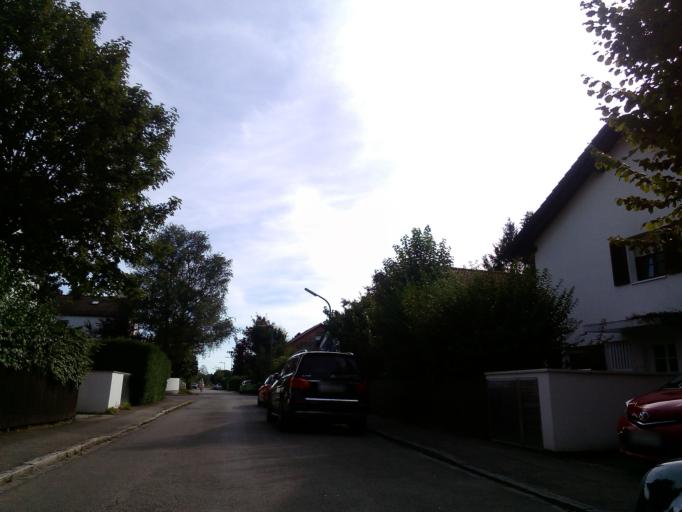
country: DE
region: Bavaria
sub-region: Upper Bavaria
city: Pullach im Isartal
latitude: 48.0771
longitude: 11.5079
